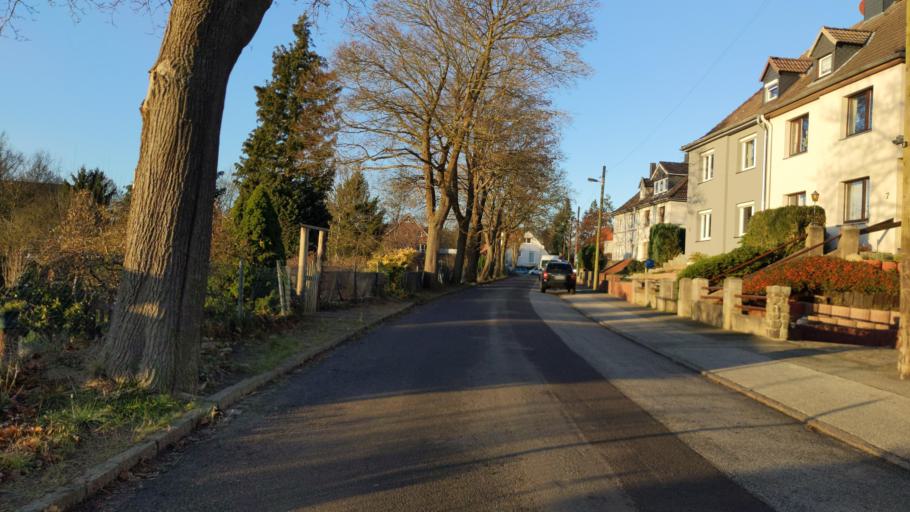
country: DE
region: Mecklenburg-Vorpommern
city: Selmsdorf
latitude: 53.8838
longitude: 10.7887
